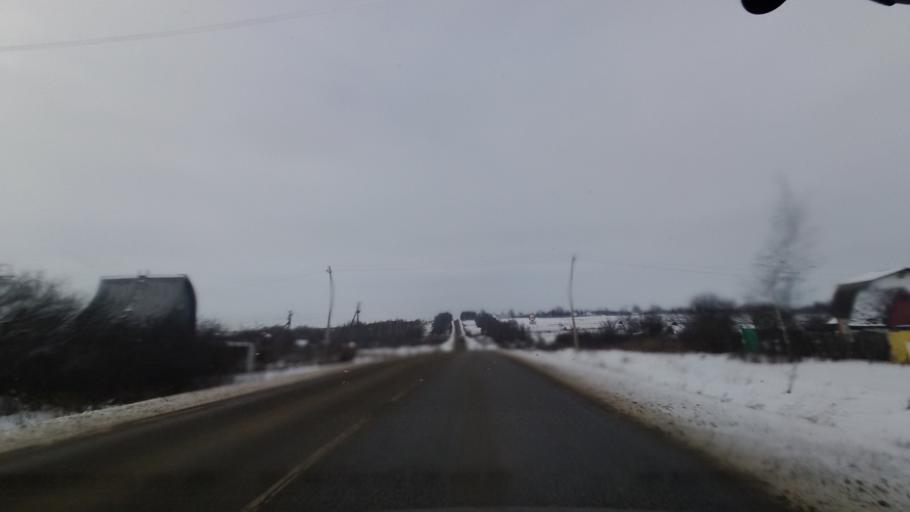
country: RU
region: Tula
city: Bogoroditsk
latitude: 53.7637
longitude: 38.0935
